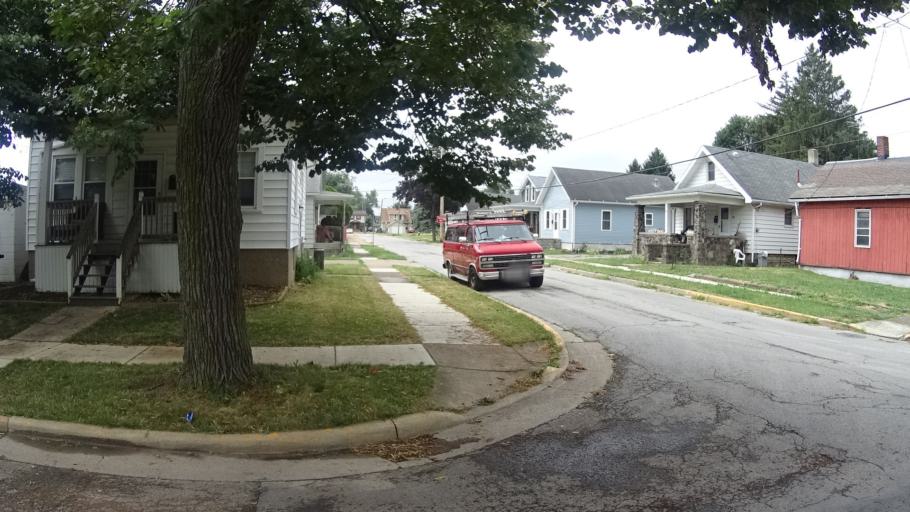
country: US
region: Ohio
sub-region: Erie County
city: Sandusky
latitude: 41.4507
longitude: -82.6924
